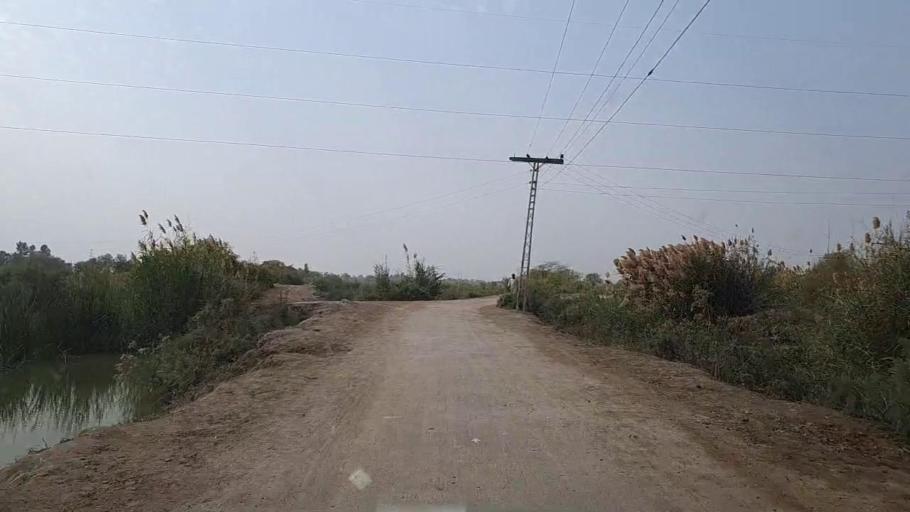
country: PK
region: Sindh
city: Mirwah Gorchani
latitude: 25.3603
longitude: 69.0382
